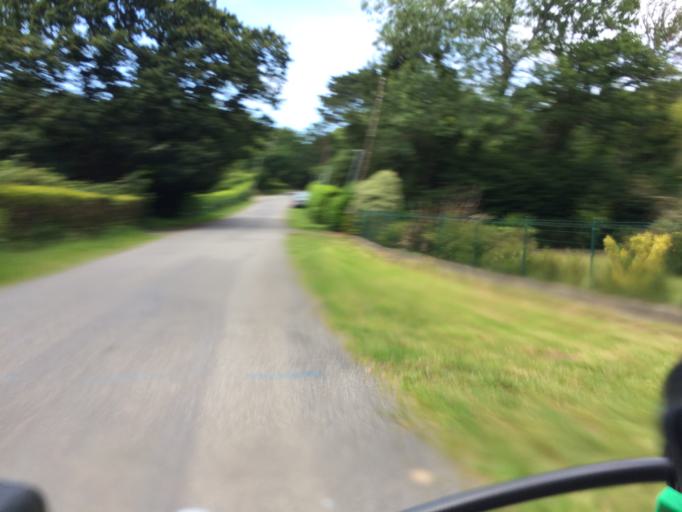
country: FR
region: Brittany
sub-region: Departement du Finistere
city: Logonna-Daoulas
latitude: 48.3197
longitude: -4.2858
